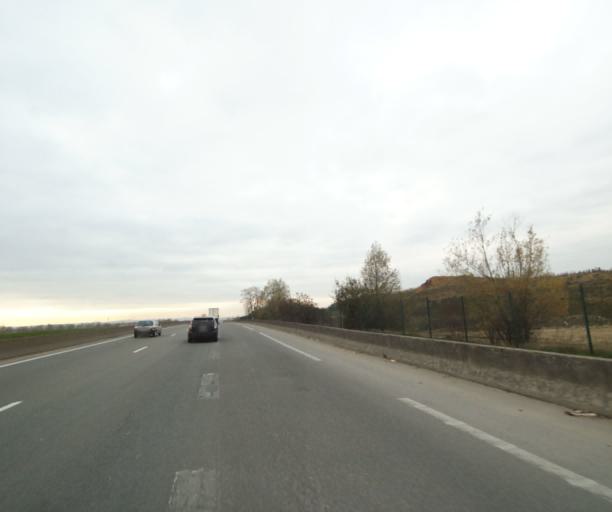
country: FR
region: Ile-de-France
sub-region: Departement du Val-d'Oise
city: Le Thillay
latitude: 48.9914
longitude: 2.4763
